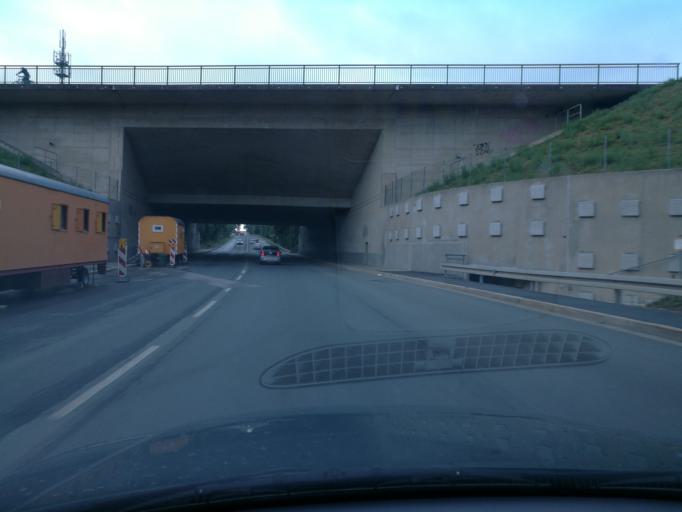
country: DE
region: Bavaria
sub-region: Regierungsbezirk Mittelfranken
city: Obermichelbach
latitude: 49.5308
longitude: 10.9647
